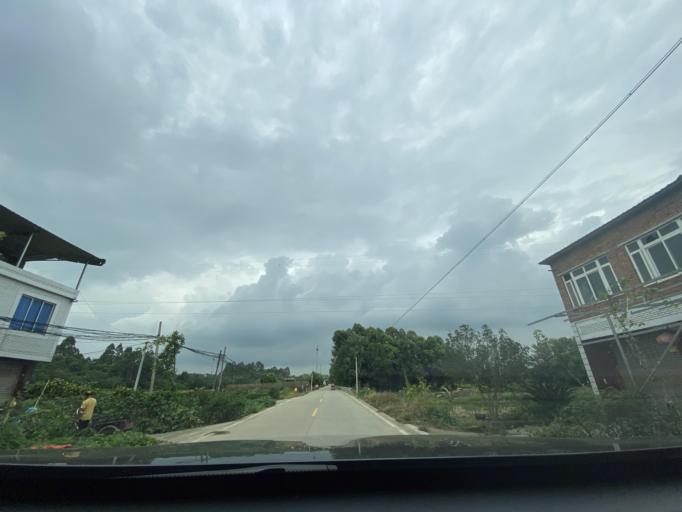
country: CN
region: Sichuan
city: Wujin
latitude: 30.3829
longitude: 103.9677
